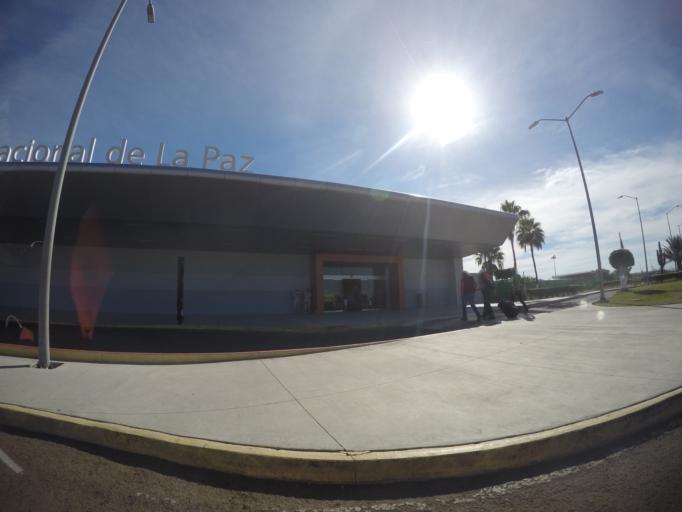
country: MX
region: Baja California Sur
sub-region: La Paz
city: La Paz
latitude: 24.2059
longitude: -110.2994
